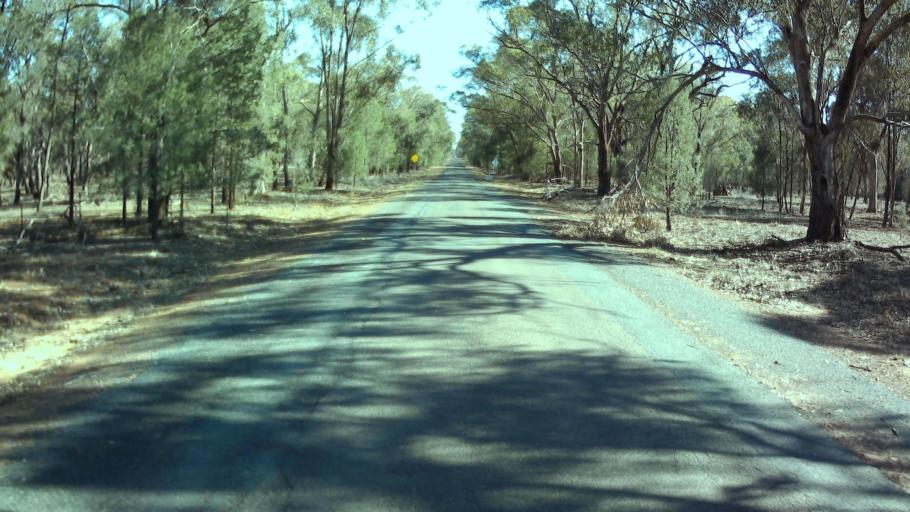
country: AU
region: New South Wales
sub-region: Weddin
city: Grenfell
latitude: -33.8148
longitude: 147.9533
